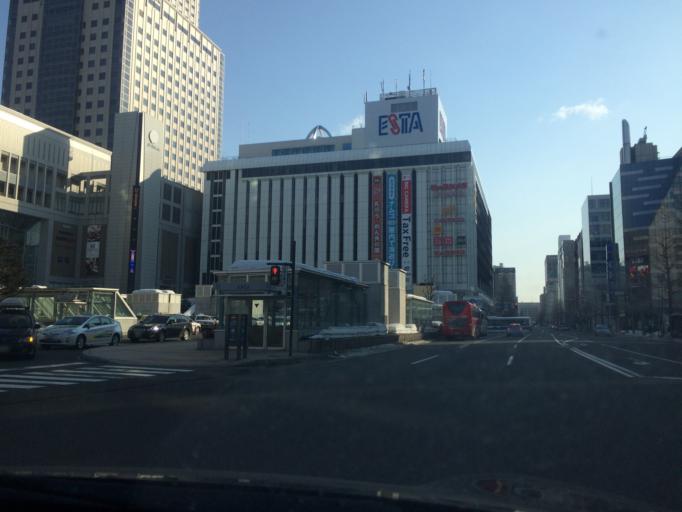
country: JP
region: Hokkaido
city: Sapporo
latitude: 43.0668
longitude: 141.3507
